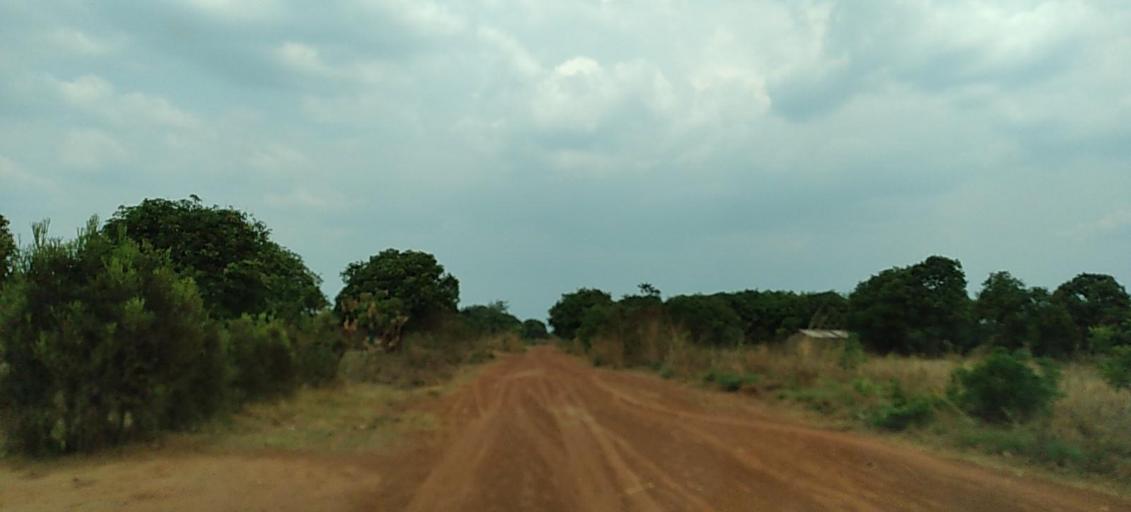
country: ZM
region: Copperbelt
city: Kalulushi
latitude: -12.8920
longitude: 28.0768
